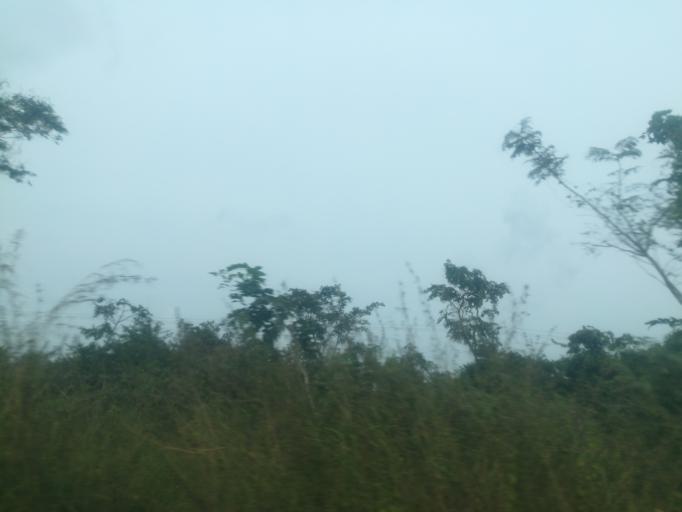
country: NG
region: Ogun
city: Ayetoro
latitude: 7.2791
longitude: 3.0938
